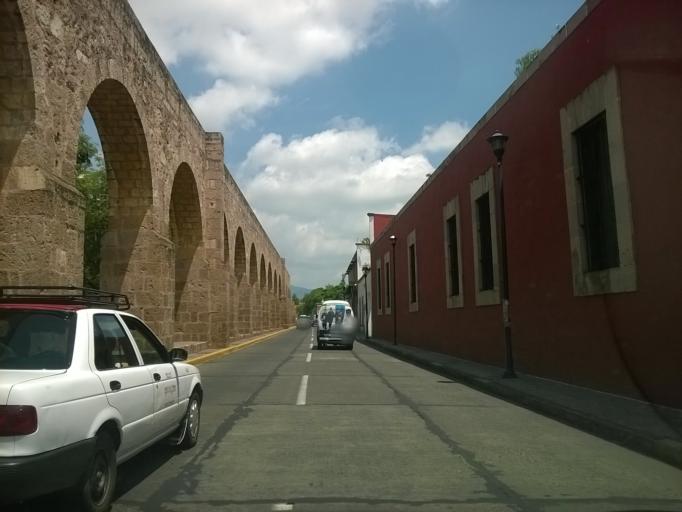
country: MX
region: Michoacan
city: Morelia
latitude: 19.7010
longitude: -101.1802
